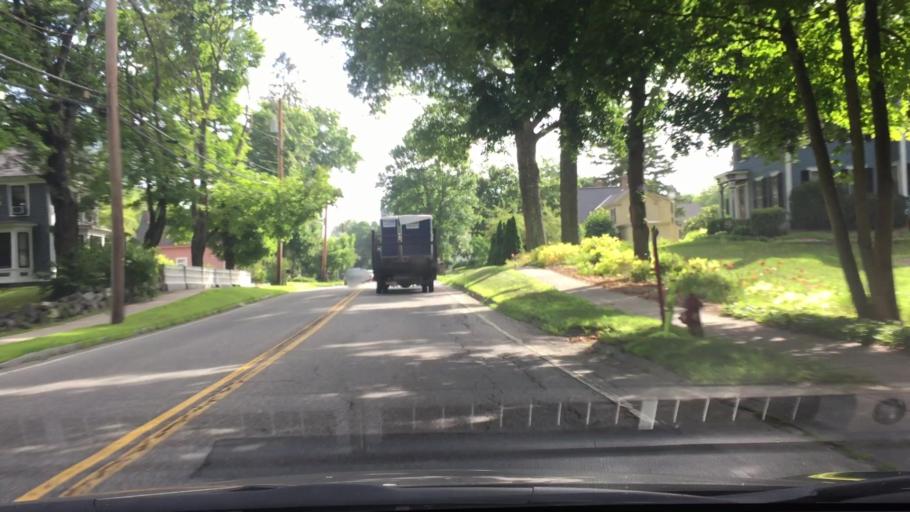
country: US
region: Massachusetts
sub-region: Middlesex County
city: Acton
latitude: 42.4842
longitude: -71.4359
